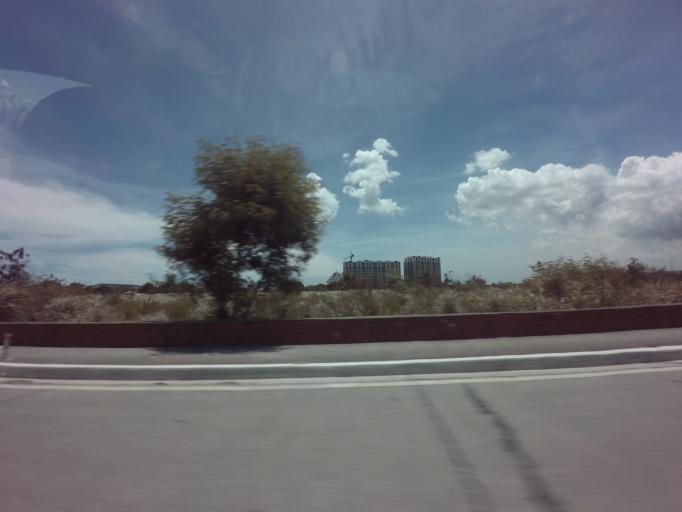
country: PH
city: Sambayanihan People's Village
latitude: 14.4863
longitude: 120.9975
